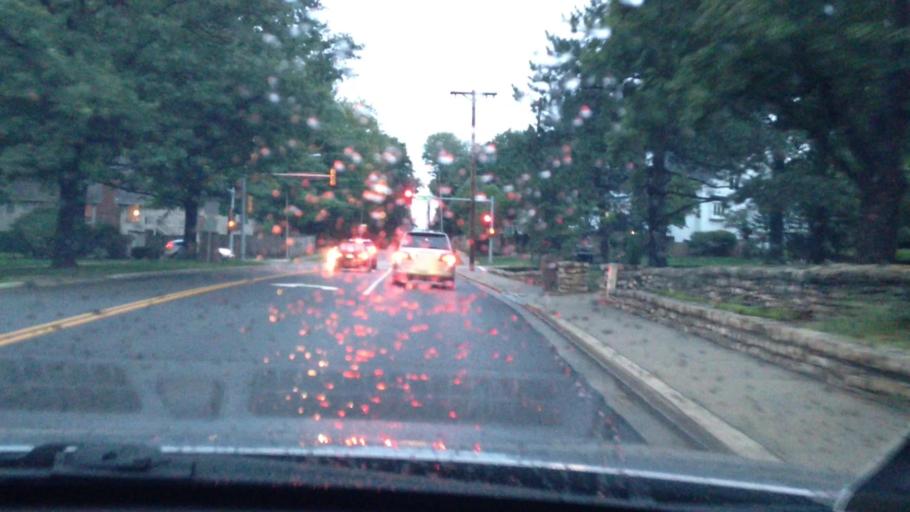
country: US
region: Kansas
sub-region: Johnson County
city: Prairie Village
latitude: 38.9786
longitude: -94.6482
